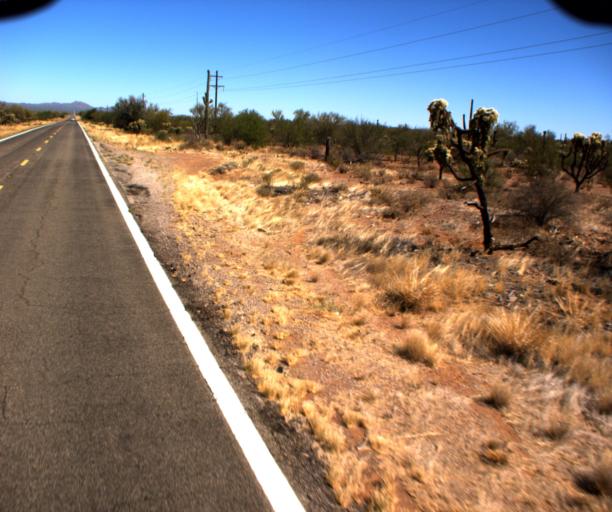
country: US
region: Arizona
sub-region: Pima County
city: Sells
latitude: 32.0503
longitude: -112.0255
